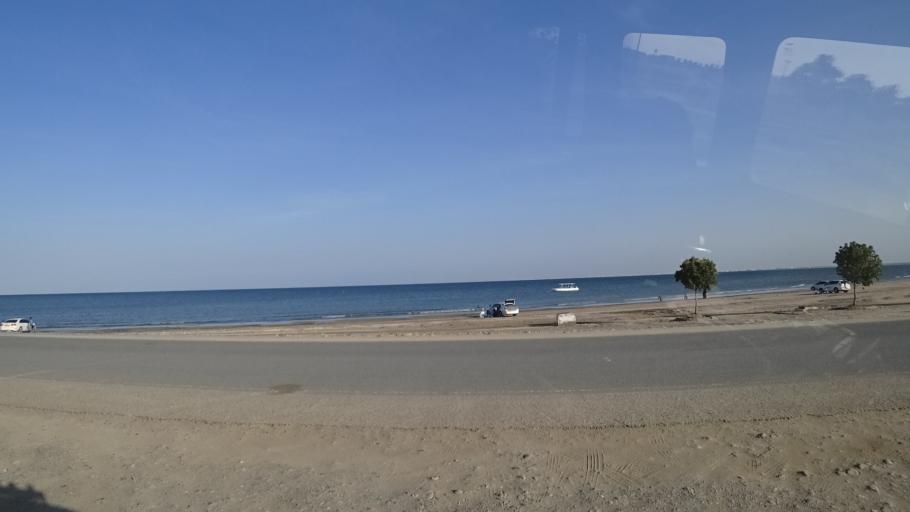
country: OM
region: Al Batinah
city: Barka'
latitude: 23.7792
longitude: 57.7903
